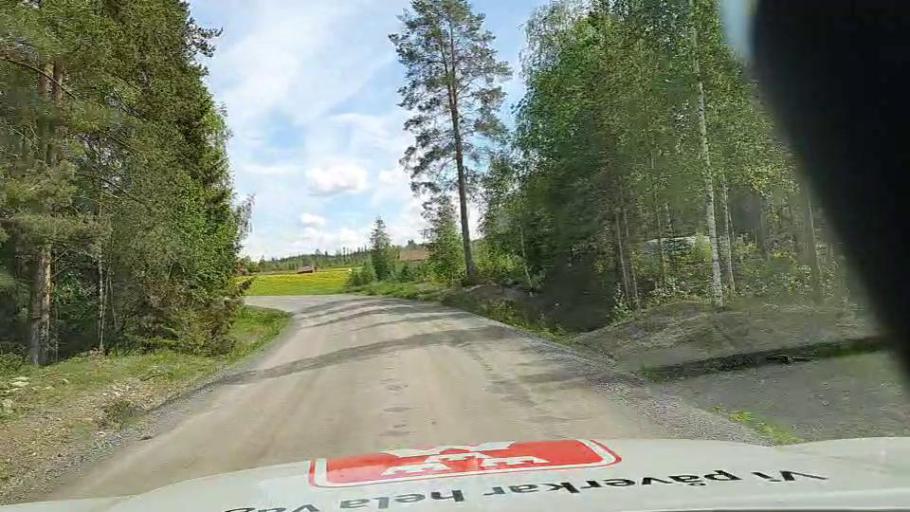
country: SE
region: Jaemtland
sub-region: OEstersunds Kommun
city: Brunflo
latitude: 63.0040
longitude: 14.7947
